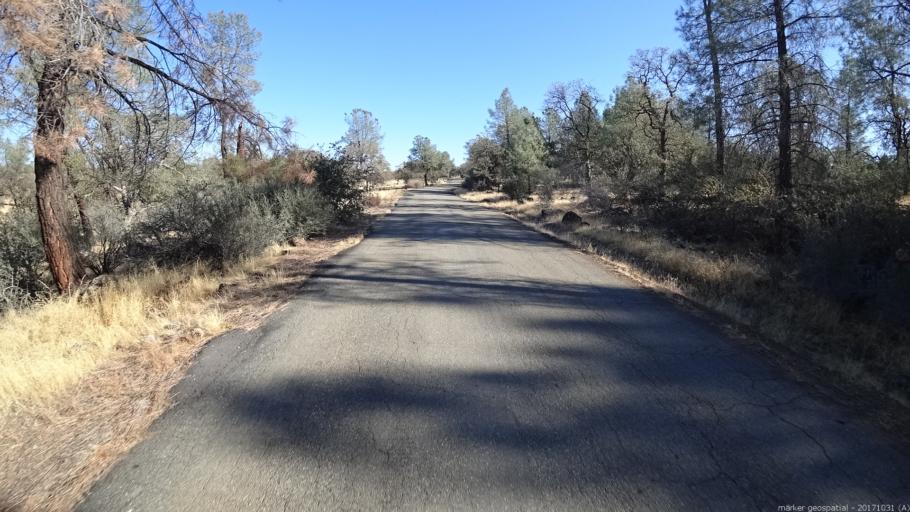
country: US
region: California
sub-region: Shasta County
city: Shingletown
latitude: 40.4594
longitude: -122.0451
